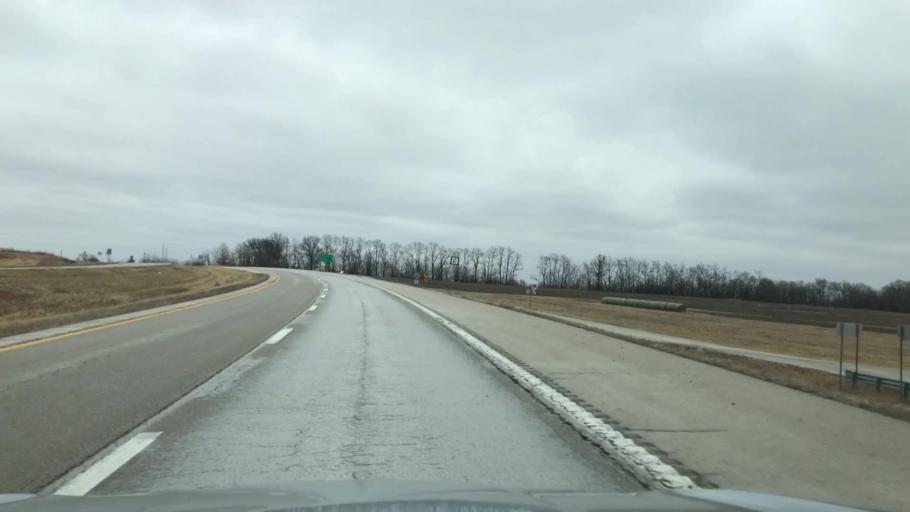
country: US
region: Missouri
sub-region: Livingston County
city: Chillicothe
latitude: 39.7367
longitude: -93.6324
